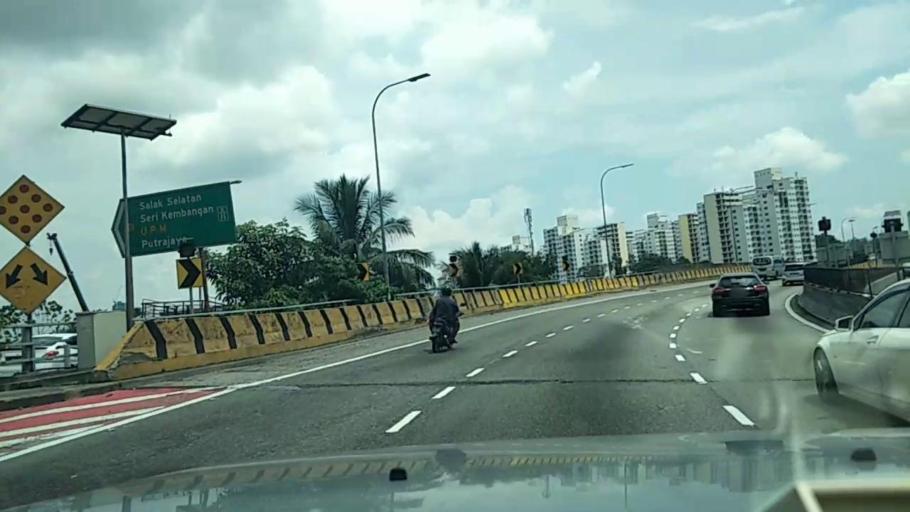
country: MY
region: Selangor
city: Kampong Baharu Balakong
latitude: 3.0673
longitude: 101.7092
